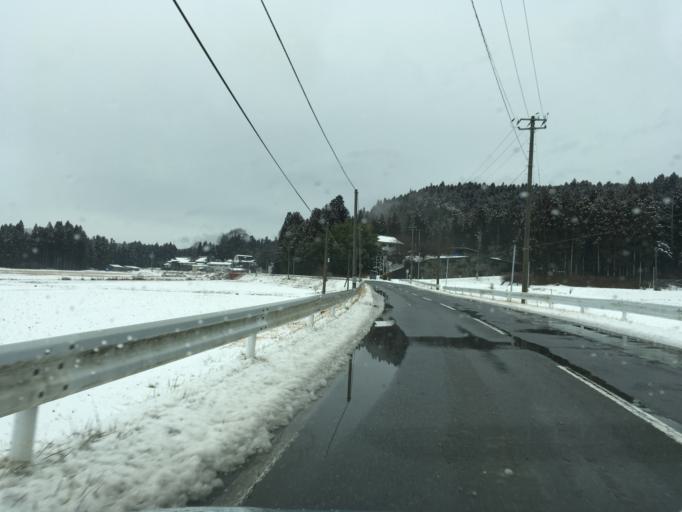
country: JP
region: Iwate
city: Ichinoseki
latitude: 38.8764
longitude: 141.2653
